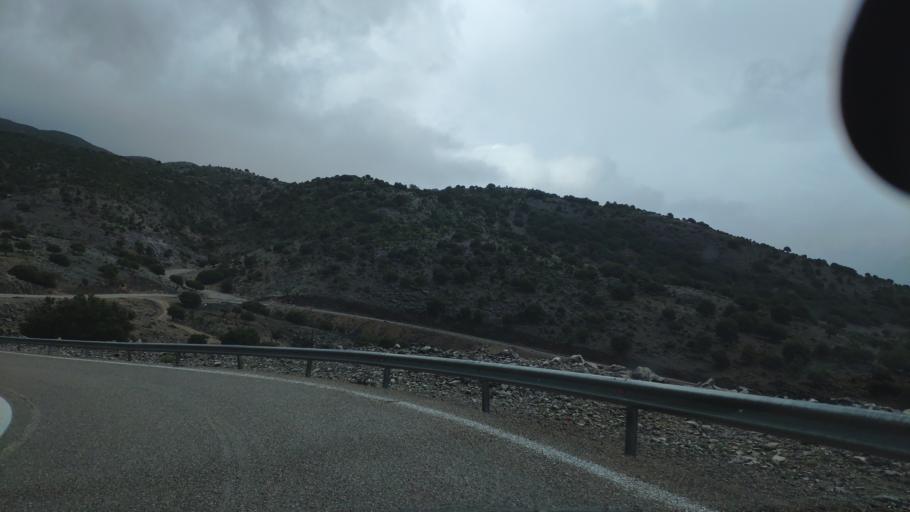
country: GR
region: Central Greece
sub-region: Nomos Evrytanias
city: Kerasochori
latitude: 39.0770
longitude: 21.3993
